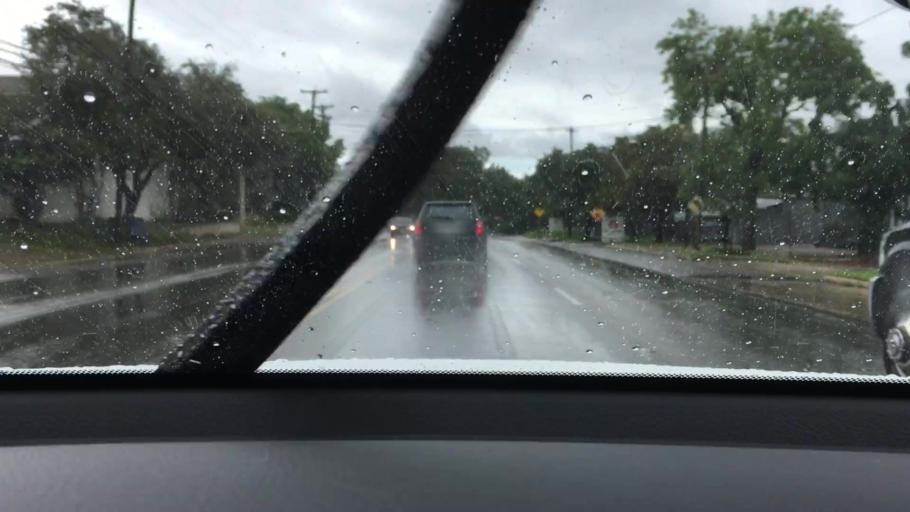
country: US
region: Texas
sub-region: Bexar County
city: Alamo Heights
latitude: 29.4843
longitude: -98.4665
